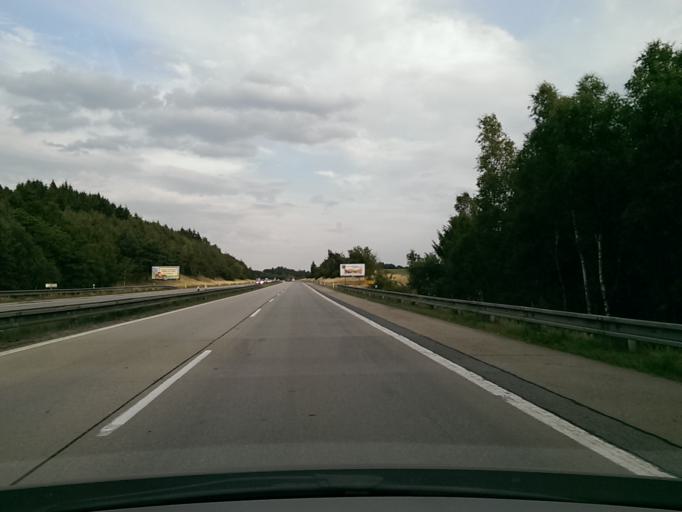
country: CZ
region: Vysocina
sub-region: Okres Zd'ar nad Sazavou
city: Velke Mezirici
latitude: 49.3402
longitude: 16.0533
